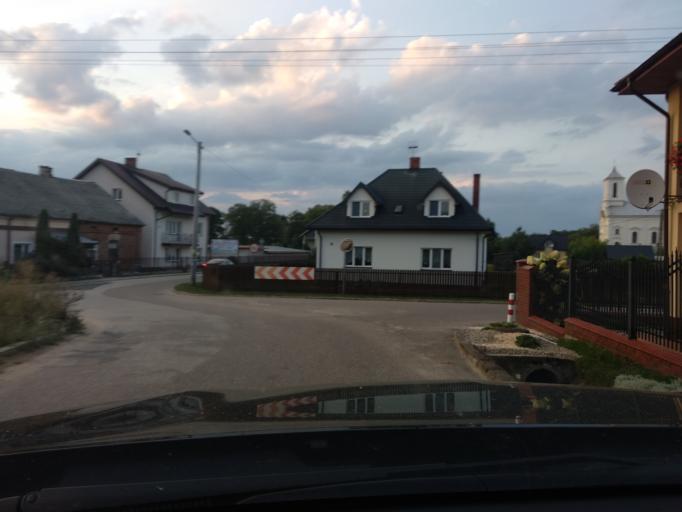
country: PL
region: Masovian Voivodeship
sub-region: Powiat pultuski
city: Obryte
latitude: 52.7555
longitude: 21.2169
